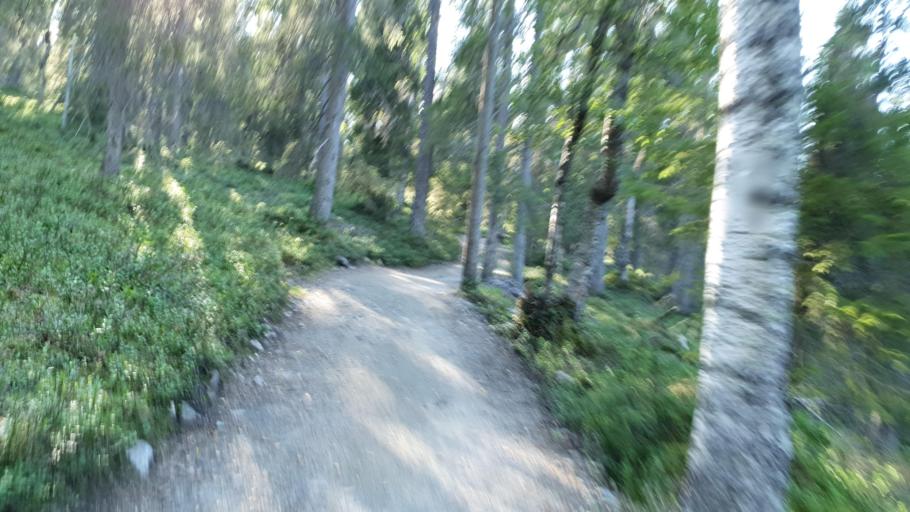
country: FI
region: Lapland
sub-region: Tunturi-Lappi
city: Kolari
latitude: 67.5970
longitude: 24.2257
